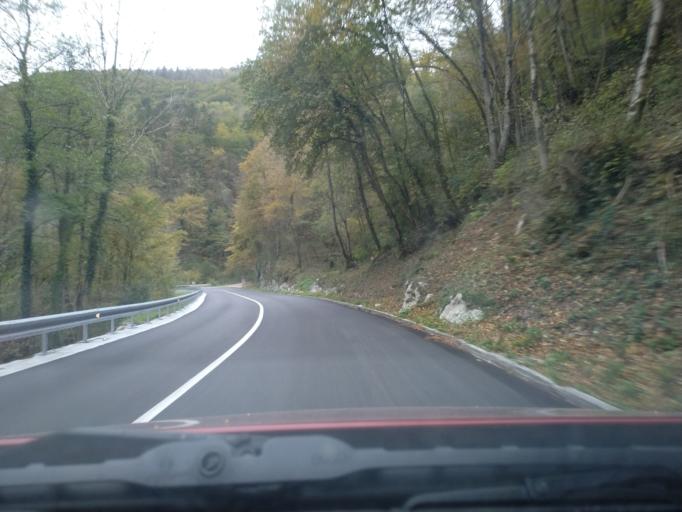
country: SI
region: Tolmin
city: Tolmin
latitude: 46.1413
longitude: 13.7147
